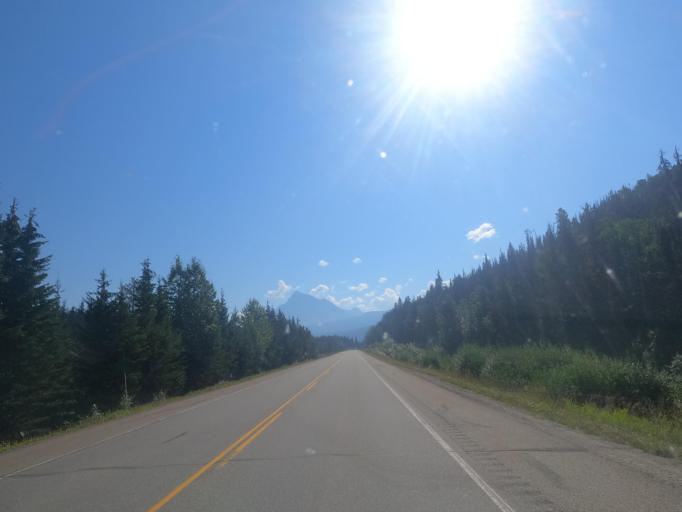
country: CA
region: Alberta
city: Jasper Park Lodge
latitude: 52.8589
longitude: -118.6356
